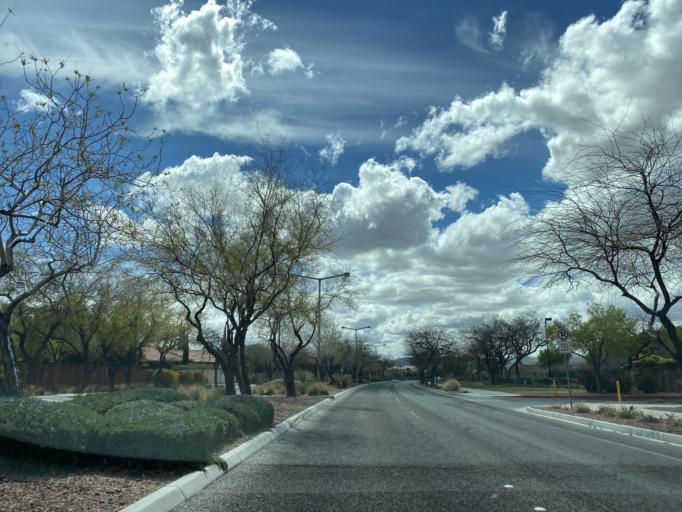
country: US
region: Nevada
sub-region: Clark County
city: Summerlin South
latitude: 36.1377
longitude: -115.3332
